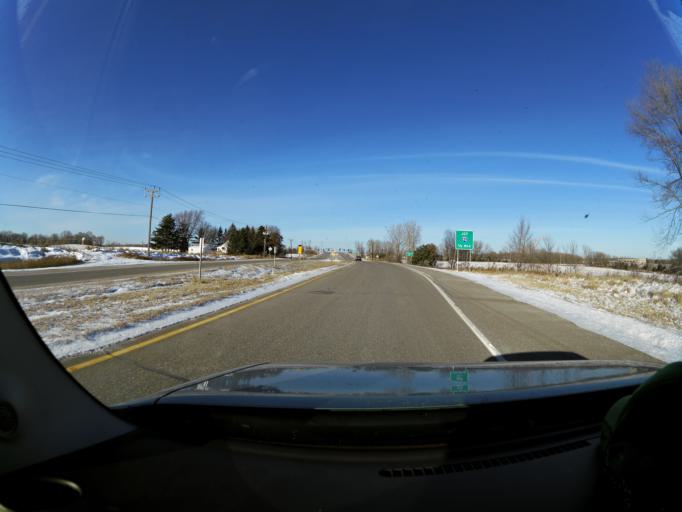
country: US
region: Minnesota
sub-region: Washington County
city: Lake Elmo
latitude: 44.9431
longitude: -92.8626
